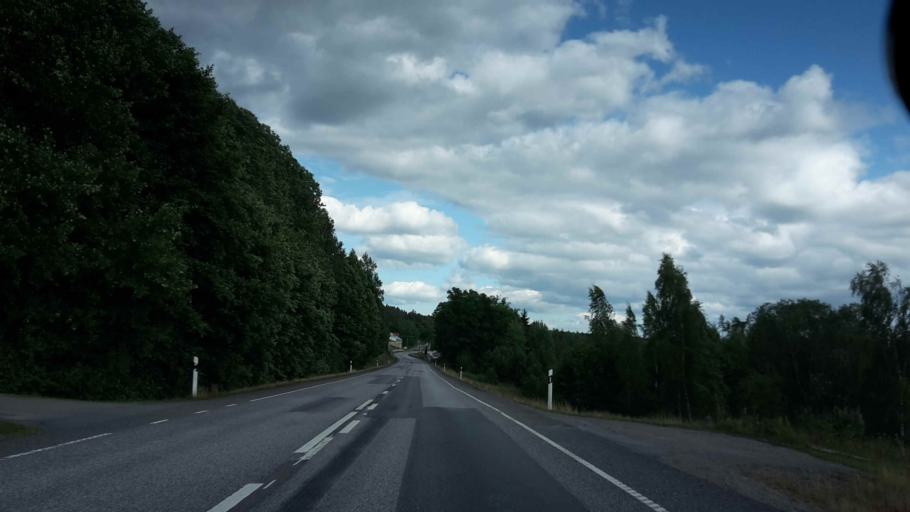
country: SE
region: OEstergoetland
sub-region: Linkopings Kommun
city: Ljungsbro
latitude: 58.7893
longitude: 15.4861
